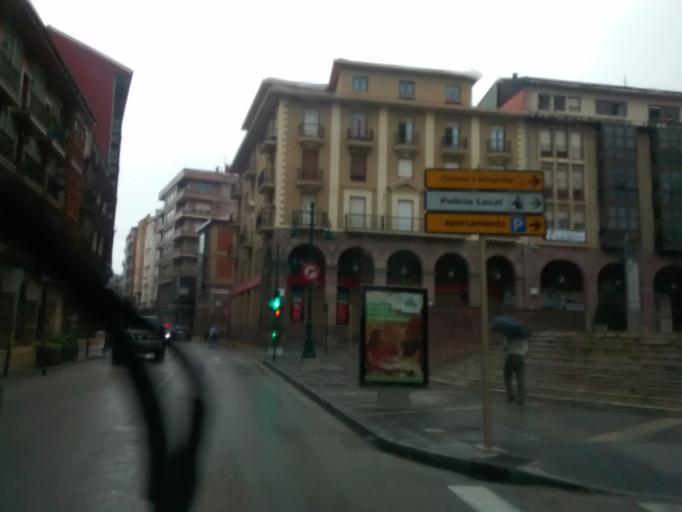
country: ES
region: Cantabria
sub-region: Provincia de Cantabria
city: Torrelavega
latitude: 43.3505
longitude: -4.0495
